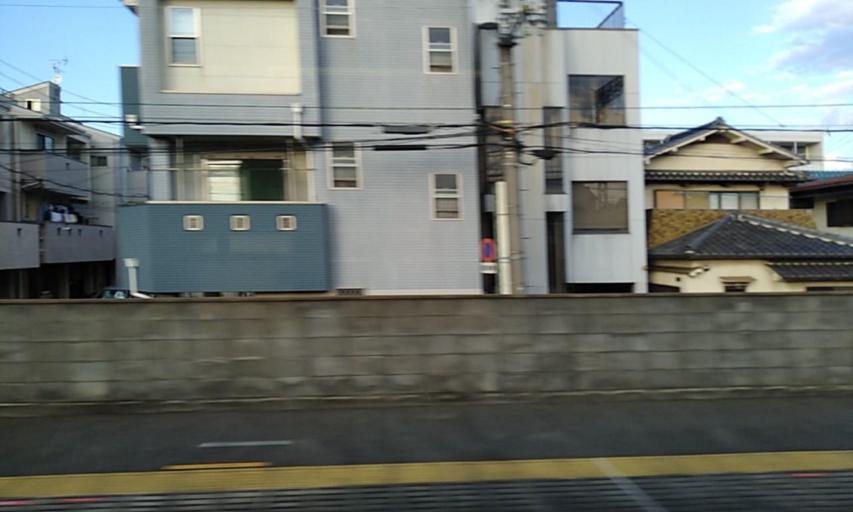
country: JP
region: Osaka
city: Sakai
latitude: 34.5612
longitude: 135.4980
